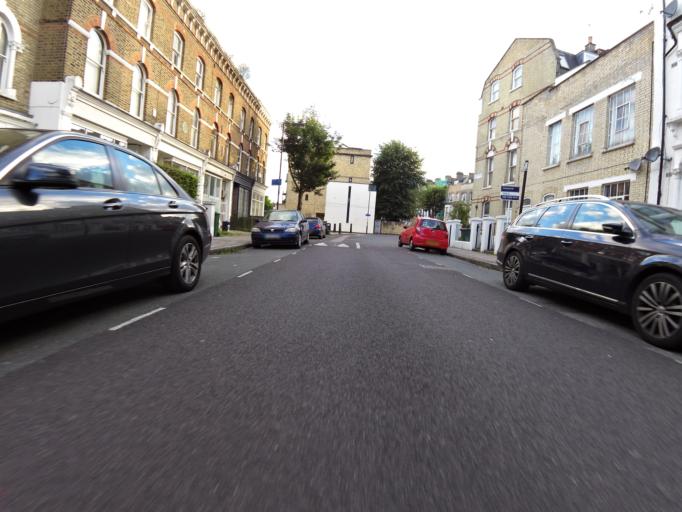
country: GB
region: England
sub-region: Greater London
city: Holloway
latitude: 51.5650
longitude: -0.1262
